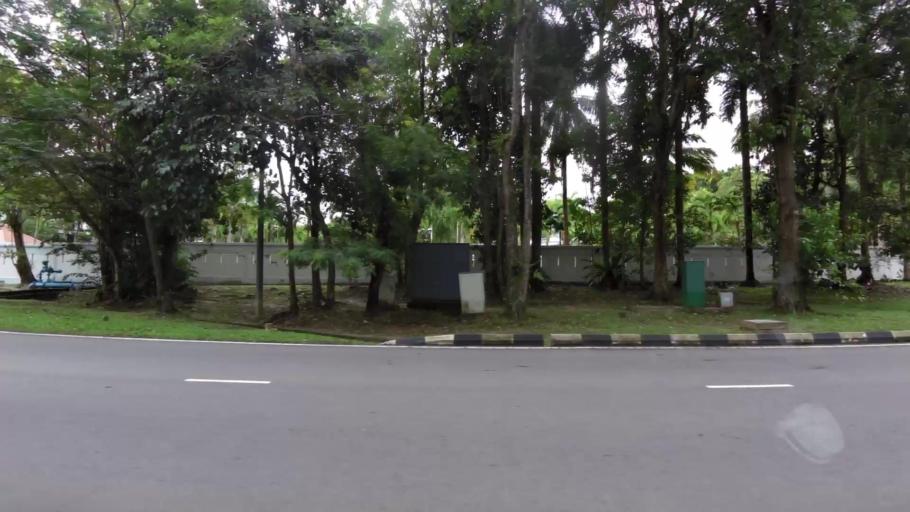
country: BN
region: Brunei and Muara
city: Bandar Seri Begawan
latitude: 4.9103
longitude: 114.9313
